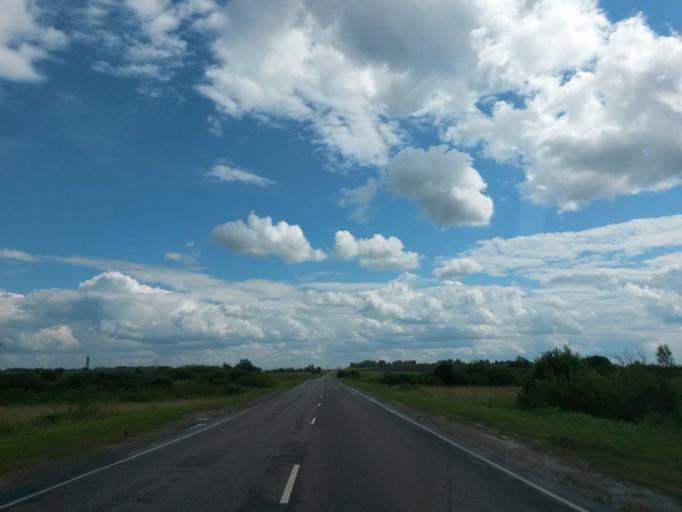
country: RU
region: Jaroslavl
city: Dubki
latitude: 57.1985
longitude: 40.3417
